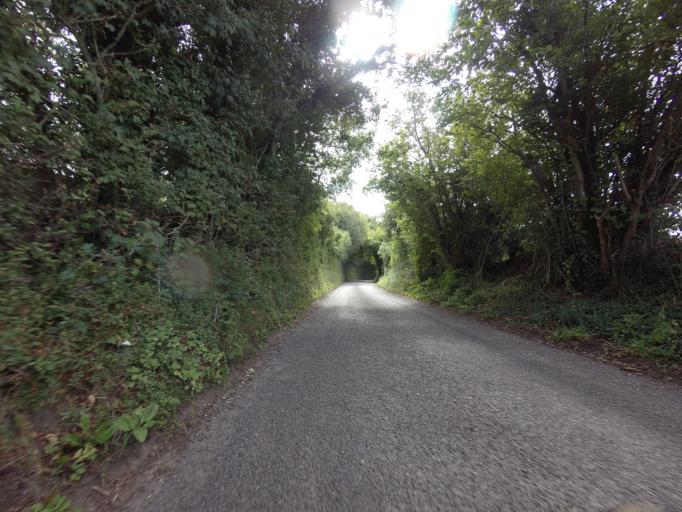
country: GB
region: England
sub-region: Greater London
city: Orpington
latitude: 51.3711
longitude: 0.1304
